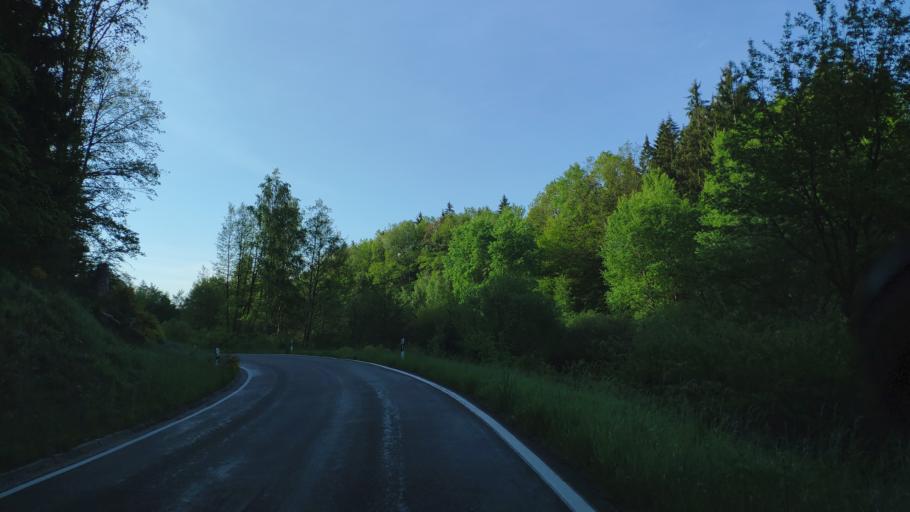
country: DE
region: Rheinland-Pfalz
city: Ludwigswinkel
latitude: 49.0940
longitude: 7.6739
